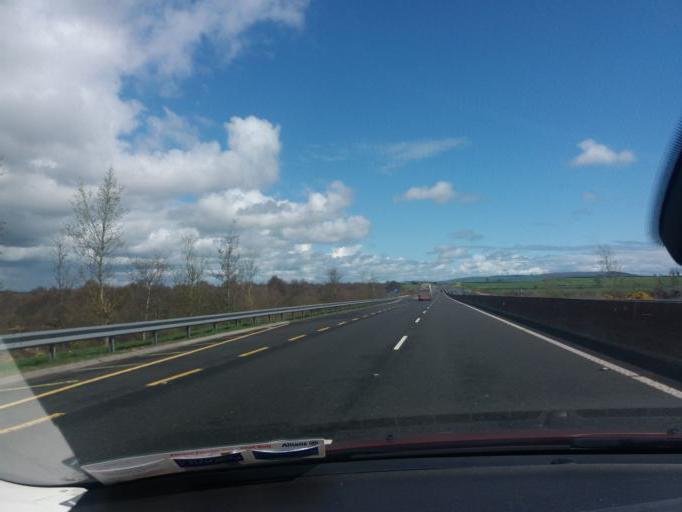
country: IE
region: Munster
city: Thurles
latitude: 52.6934
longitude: -7.6607
